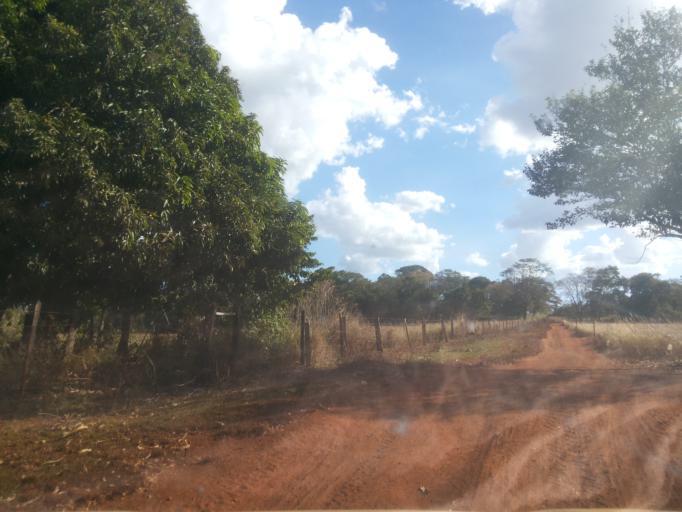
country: BR
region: Minas Gerais
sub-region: Capinopolis
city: Capinopolis
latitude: -18.6021
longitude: -49.4890
